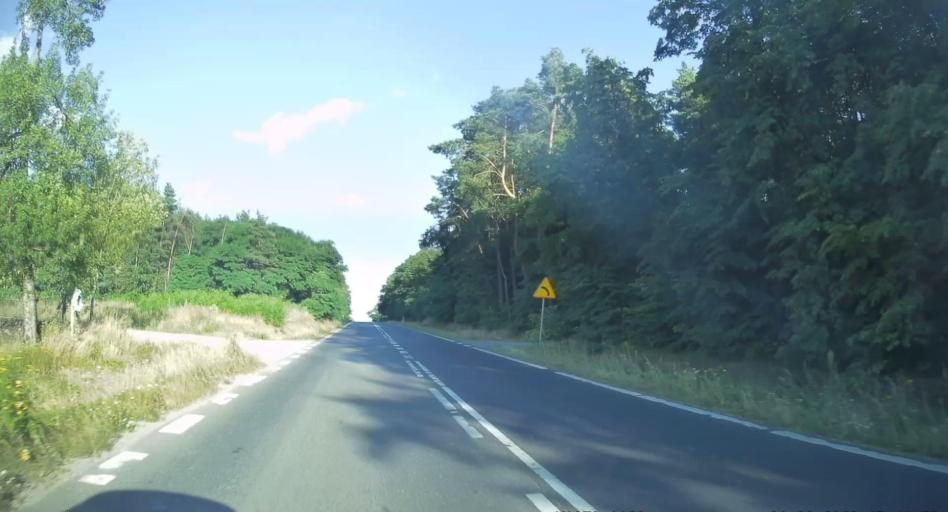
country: PL
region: Lodz Voivodeship
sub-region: Powiat rawski
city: Biala Rawska
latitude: 51.8010
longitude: 20.5130
